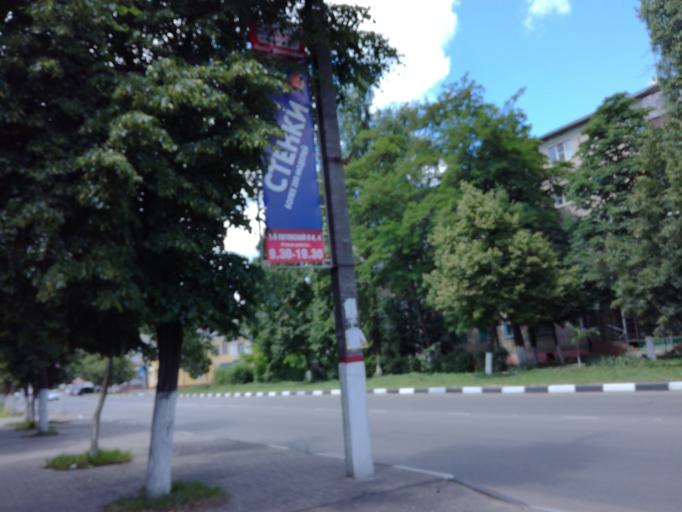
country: RU
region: Kursk
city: Kursk
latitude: 51.7474
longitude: 36.2387
